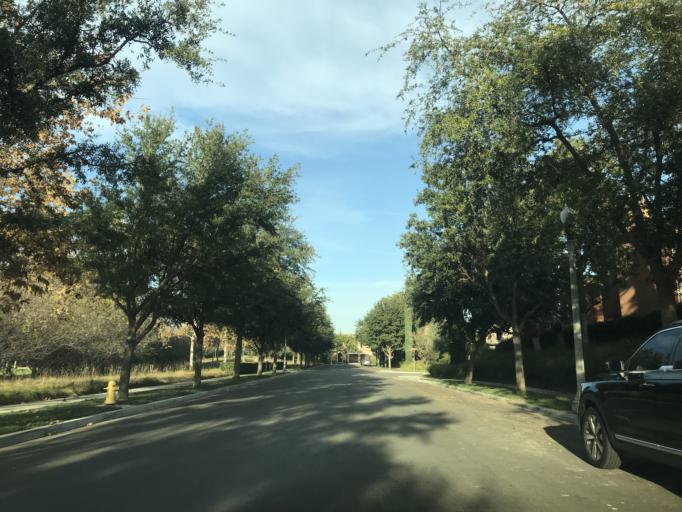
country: US
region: California
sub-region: Orange County
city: North Tustin
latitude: 33.7028
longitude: -117.7533
